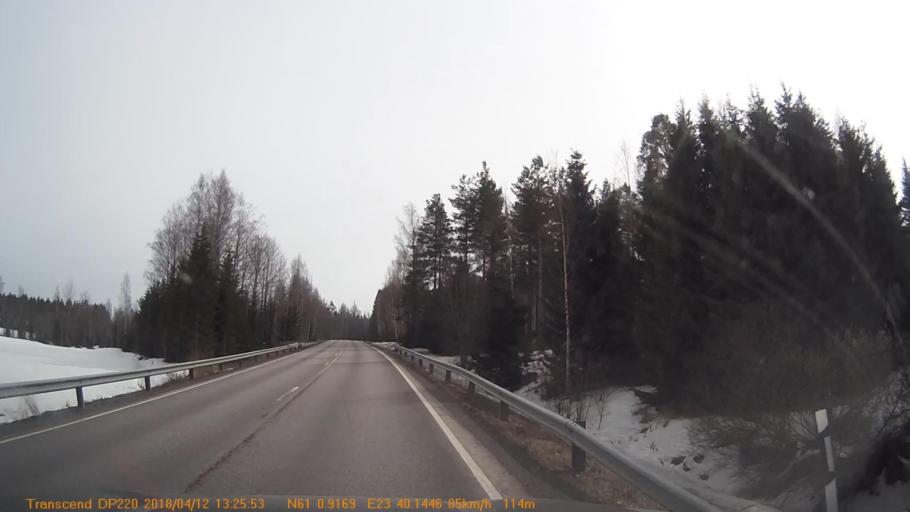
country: FI
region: Pirkanmaa
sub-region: Etelae-Pirkanmaa
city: Kylmaekoski
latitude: 61.0151
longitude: 23.6694
